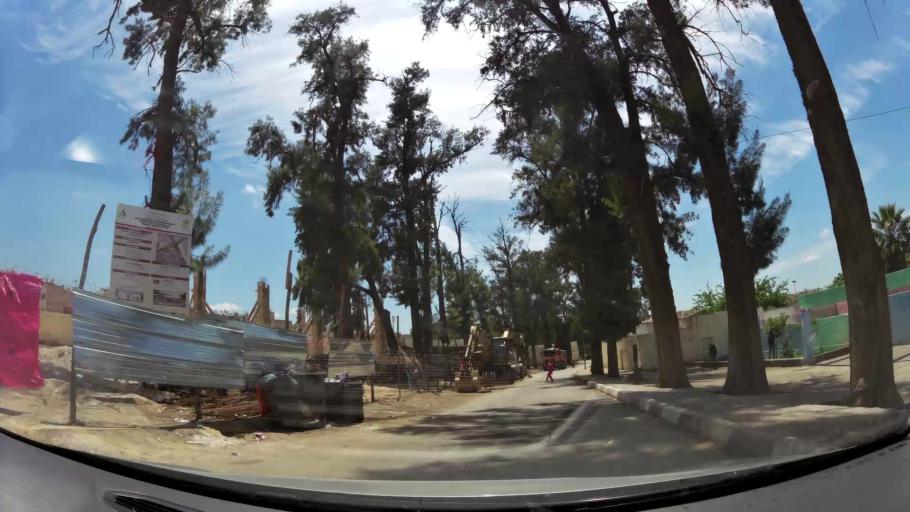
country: MA
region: Fes-Boulemane
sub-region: Fes
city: Fes
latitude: 34.0098
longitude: -4.9827
